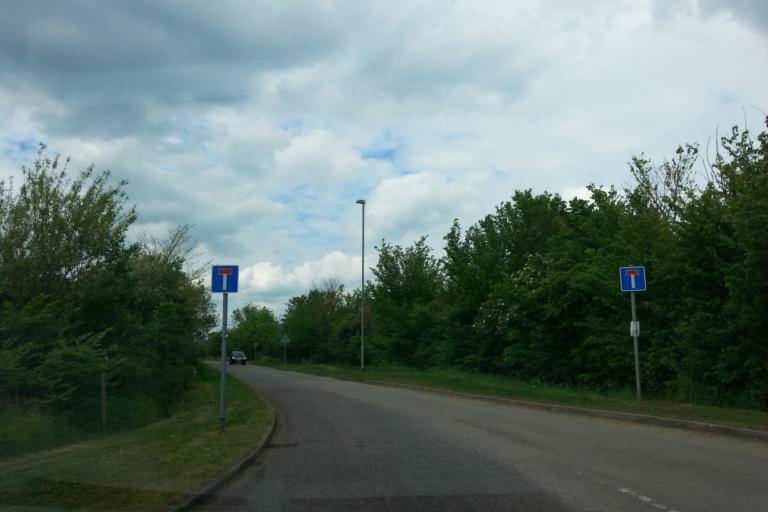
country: GB
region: England
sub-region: Cambridgeshire
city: Swavesey
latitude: 52.2821
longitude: 0.0397
